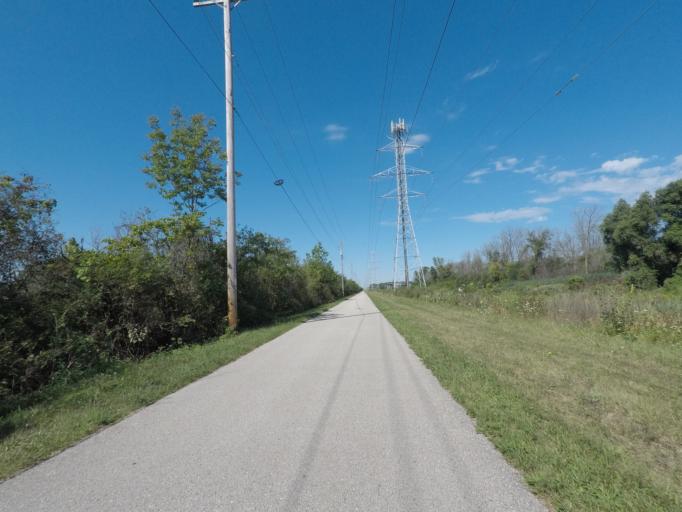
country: US
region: Wisconsin
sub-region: Waukesha County
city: New Berlin
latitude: 43.0100
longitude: -88.1463
